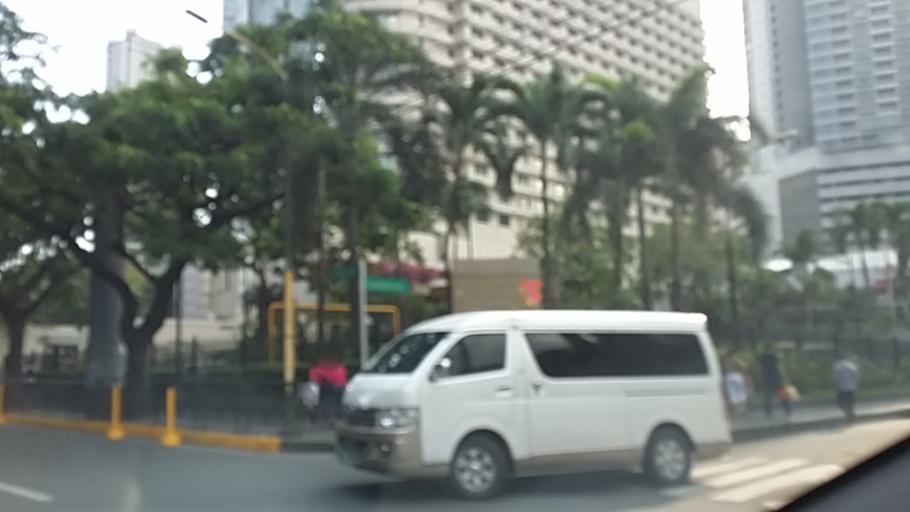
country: PH
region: Metro Manila
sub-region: Pasig
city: Pasig City
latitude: 14.5820
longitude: 121.0579
